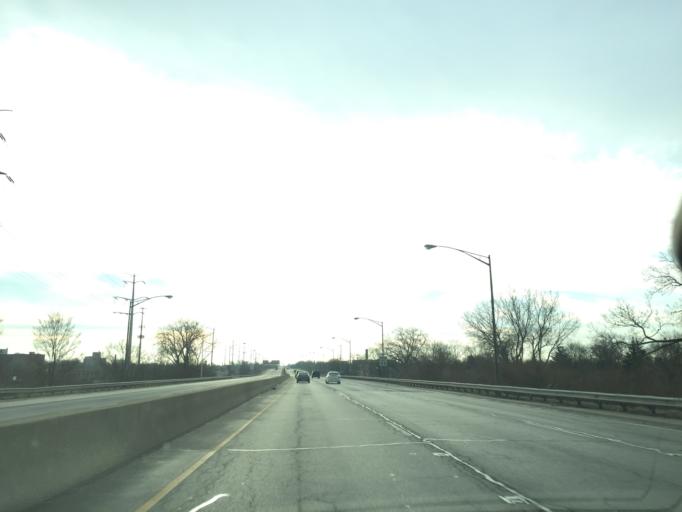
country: US
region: Illinois
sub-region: Cook County
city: Chicago
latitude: 41.7726
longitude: -87.6175
